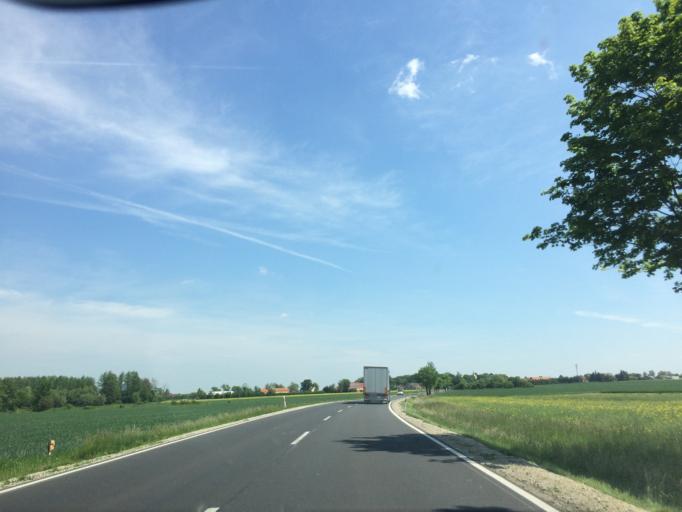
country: PL
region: Lower Silesian Voivodeship
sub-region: Powiat wroclawski
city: Sobotka
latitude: 50.9409
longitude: 16.7194
